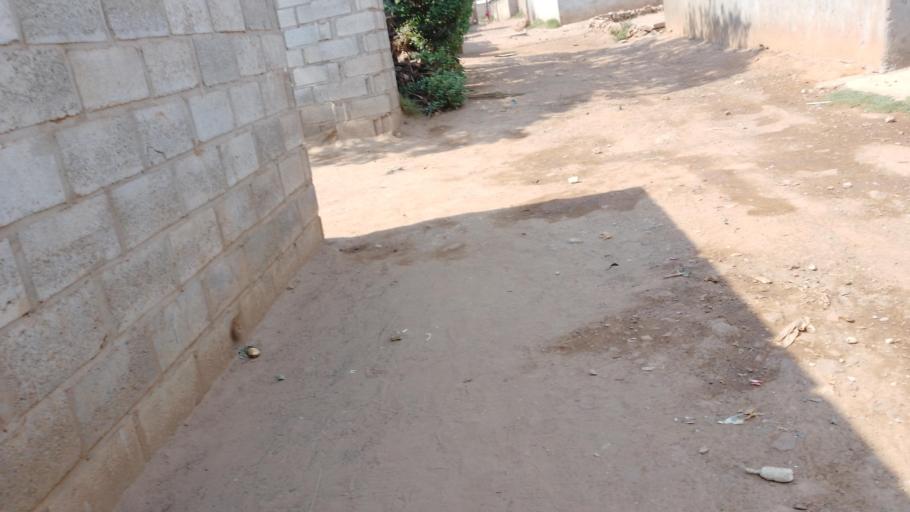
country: ZM
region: Lusaka
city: Lusaka
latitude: -15.3958
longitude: 28.3699
